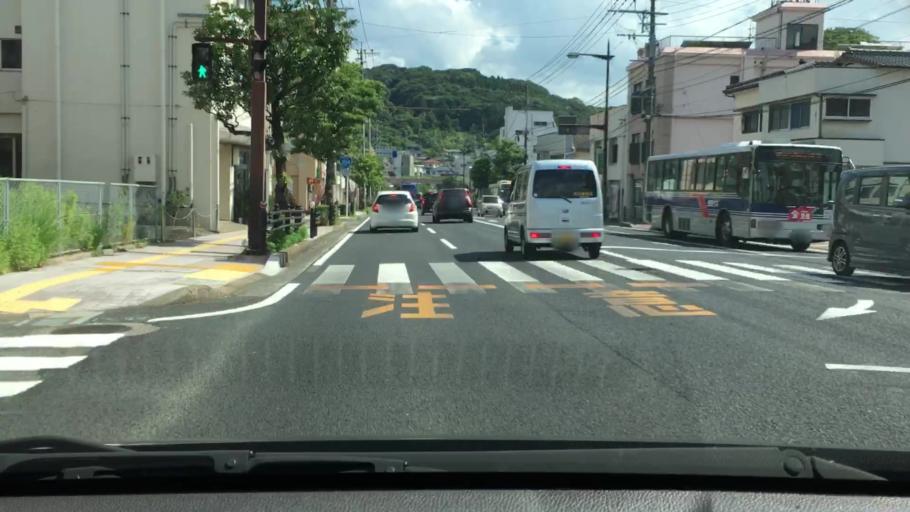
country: JP
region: Nagasaki
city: Sasebo
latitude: 33.1997
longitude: 129.7218
